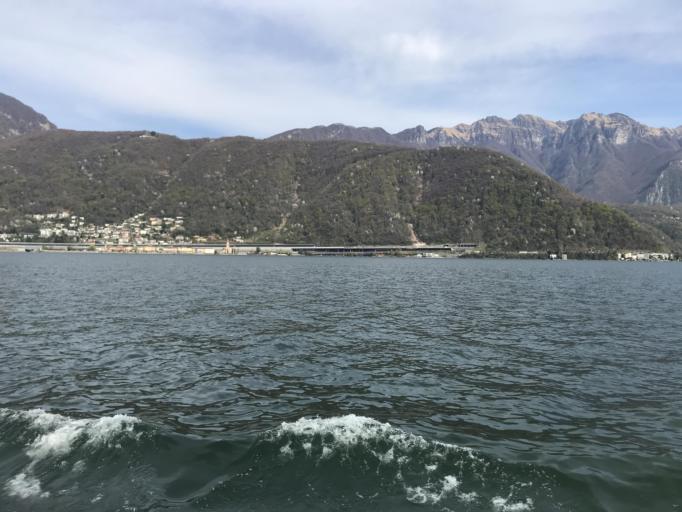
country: CH
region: Ticino
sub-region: Lugano District
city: Melide
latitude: 45.9463
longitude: 8.9484
